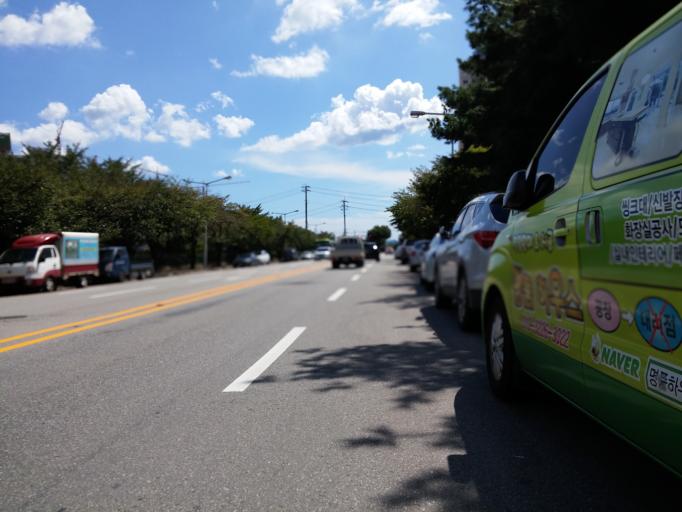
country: KR
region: Chungcheongbuk-do
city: Cheongju-si
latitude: 36.6077
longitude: 127.4970
